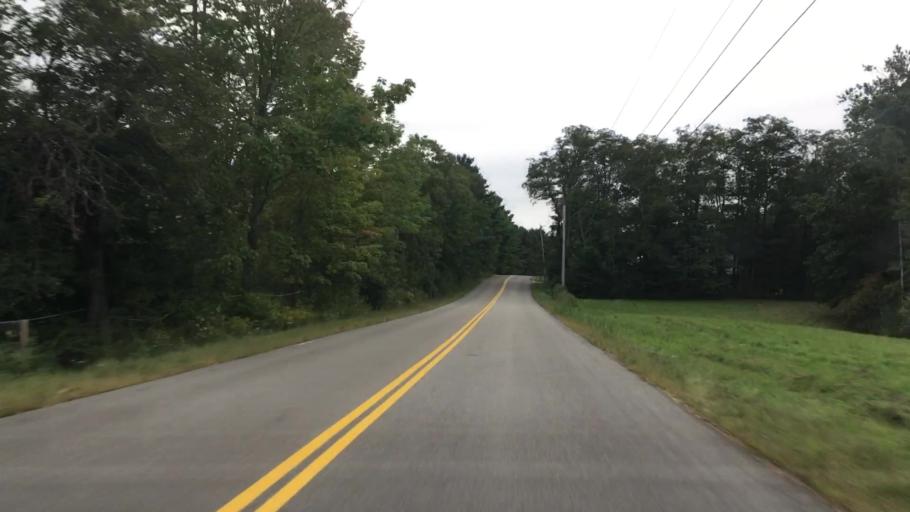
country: US
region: Maine
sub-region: Cumberland County
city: New Gloucester
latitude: 43.9163
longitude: -70.2439
